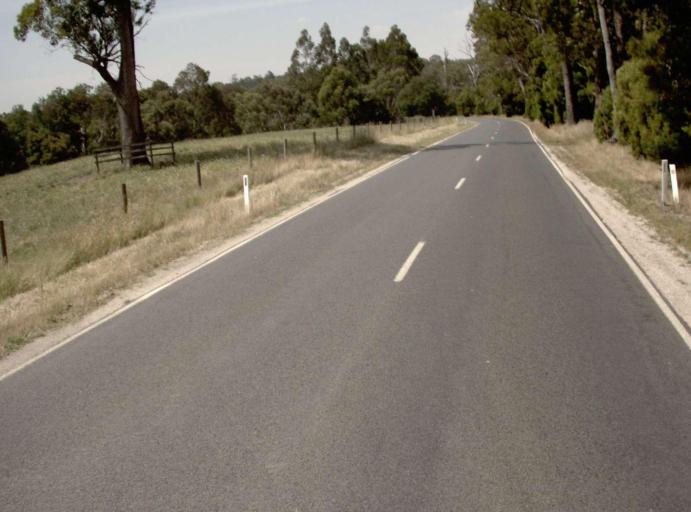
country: AU
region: Victoria
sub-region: Latrobe
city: Traralgon
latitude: -38.2843
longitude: 146.5447
